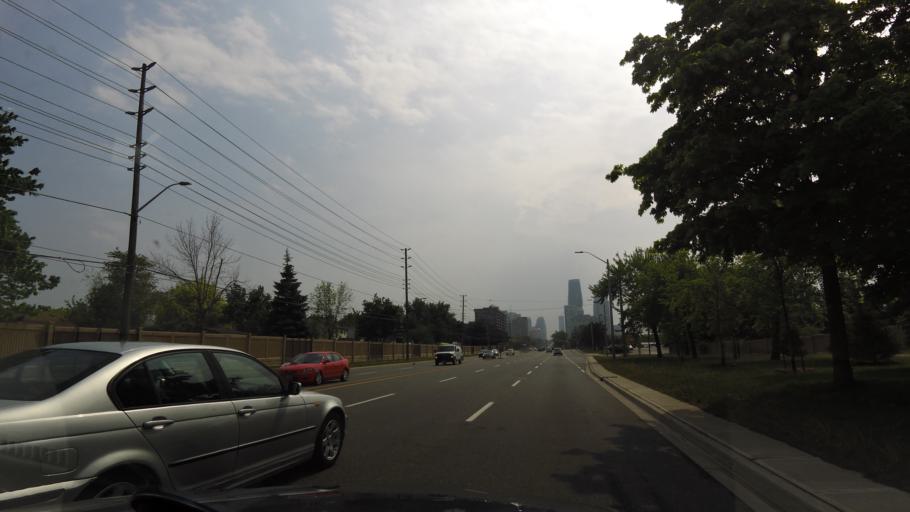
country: CA
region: Ontario
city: Mississauga
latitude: 43.6030
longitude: -79.6243
